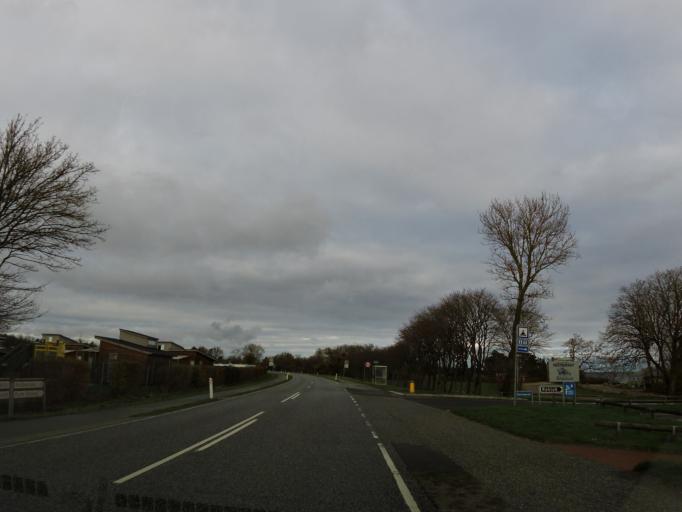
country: DK
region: Central Jutland
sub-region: Arhus Kommune
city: Malling
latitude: 55.9799
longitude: 10.2490
